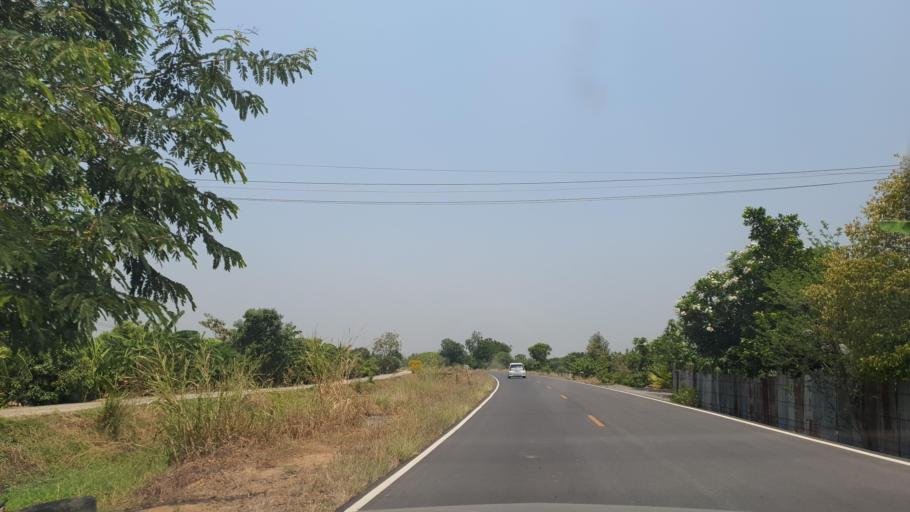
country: TH
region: Suphan Buri
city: Si Prachan
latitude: 14.6160
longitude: 100.1009
